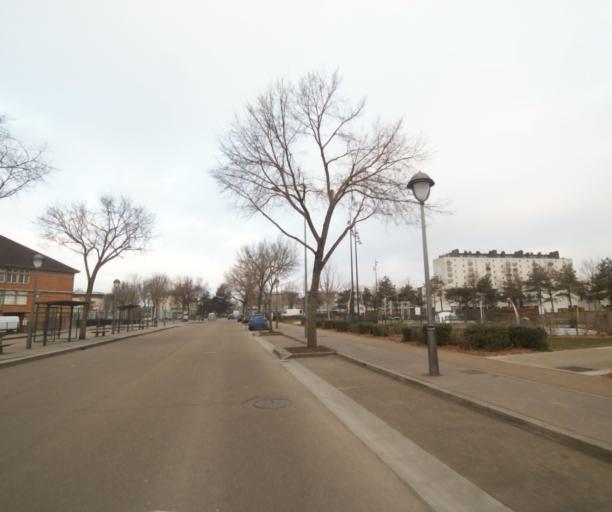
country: FR
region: Champagne-Ardenne
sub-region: Departement de la Haute-Marne
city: Bettancourt-la-Ferree
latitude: 48.6435
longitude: 4.9650
